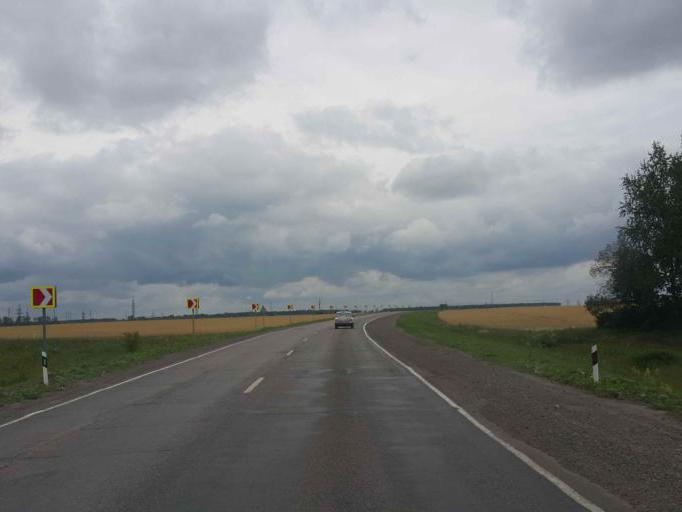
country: RU
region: Tambov
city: Komsomolets
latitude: 52.7498
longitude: 41.2953
